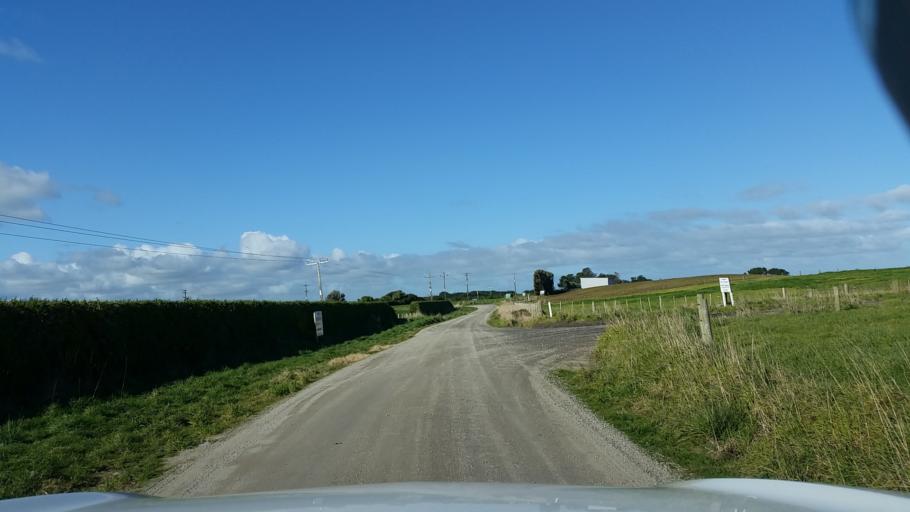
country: NZ
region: Taranaki
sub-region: South Taranaki District
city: Patea
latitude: -39.6858
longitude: 174.3946
